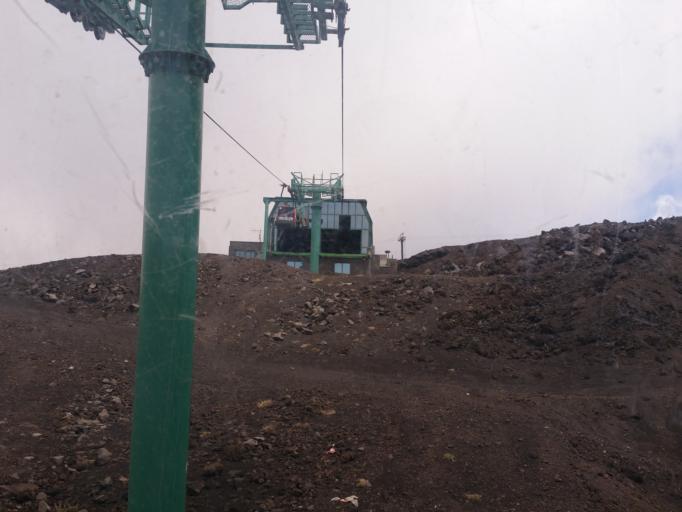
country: IT
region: Sicily
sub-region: Catania
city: Ragalna
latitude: 37.7173
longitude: 14.9999
